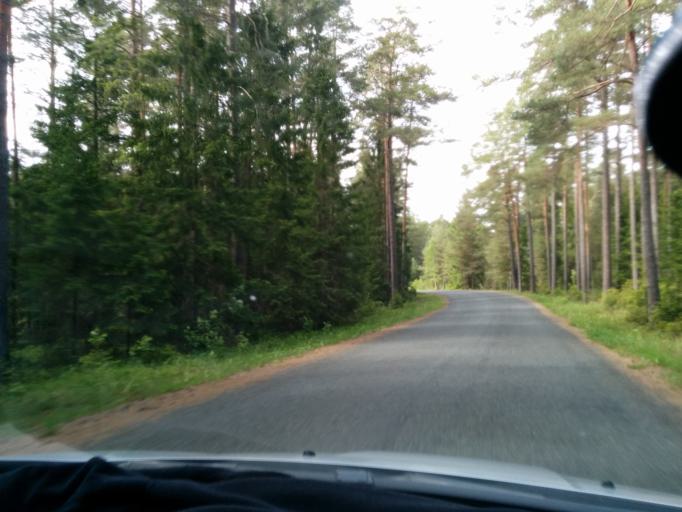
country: EE
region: Harju
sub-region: Loksa linn
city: Loksa
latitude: 59.5880
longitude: 25.5968
